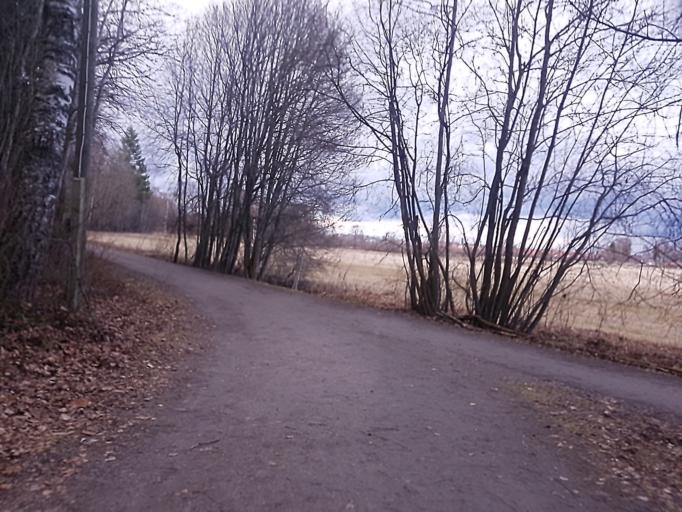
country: FI
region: Uusimaa
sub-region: Helsinki
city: Helsinki
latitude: 60.2721
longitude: 24.9377
